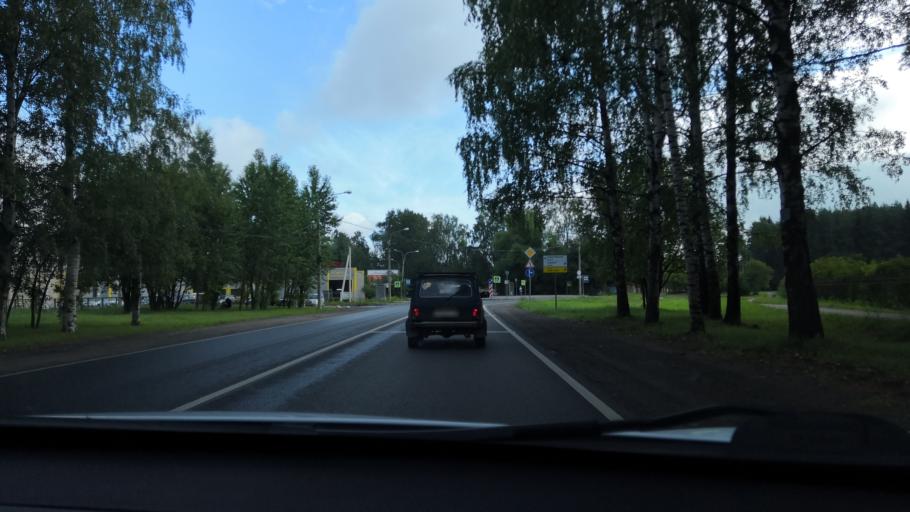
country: RU
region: St.-Petersburg
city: Pavlovsk
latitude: 59.6974
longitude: 30.4405
